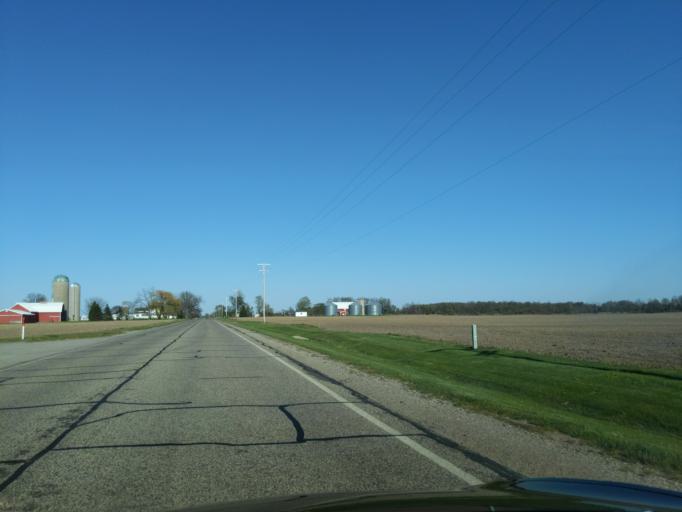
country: US
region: Michigan
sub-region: Ionia County
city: Ionia
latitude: 42.8858
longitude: -85.0214
